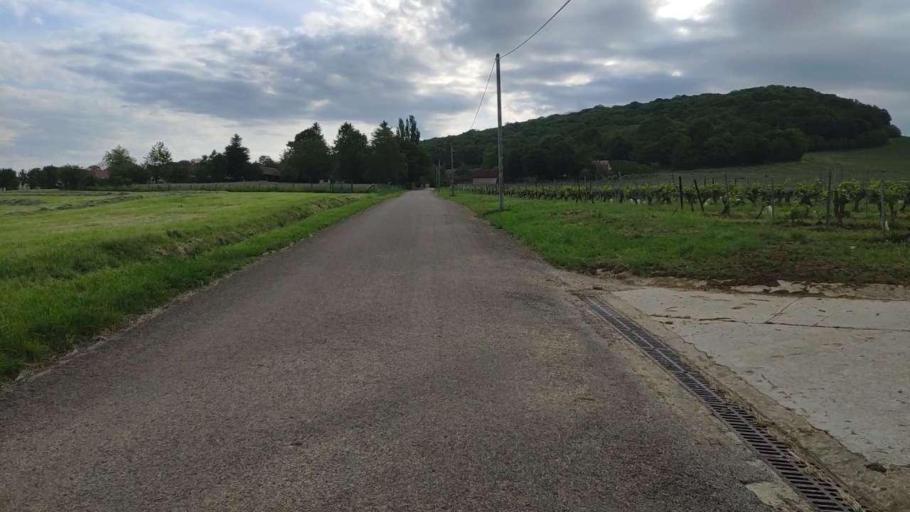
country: FR
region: Franche-Comte
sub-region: Departement du Jura
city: Perrigny
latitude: 46.7363
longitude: 5.5998
